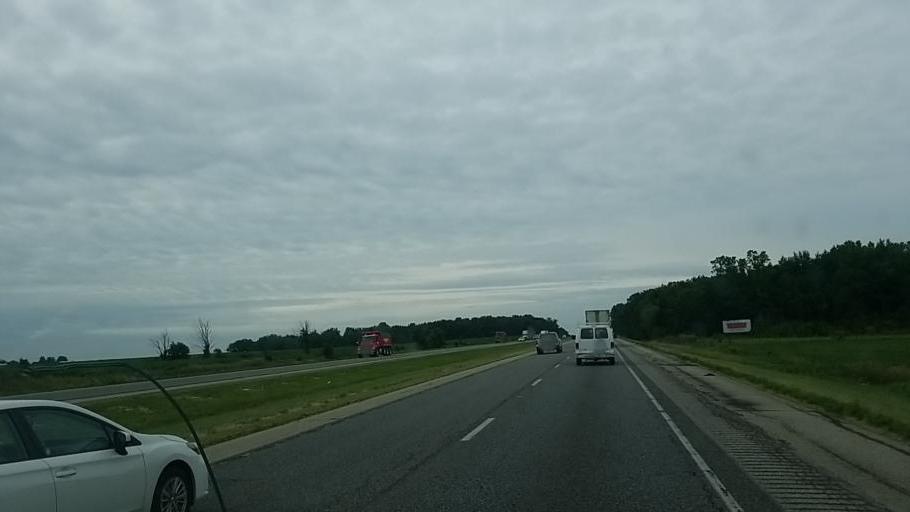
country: US
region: Indiana
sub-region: DeKalb County
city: Waterloo
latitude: 41.4721
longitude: -85.0544
